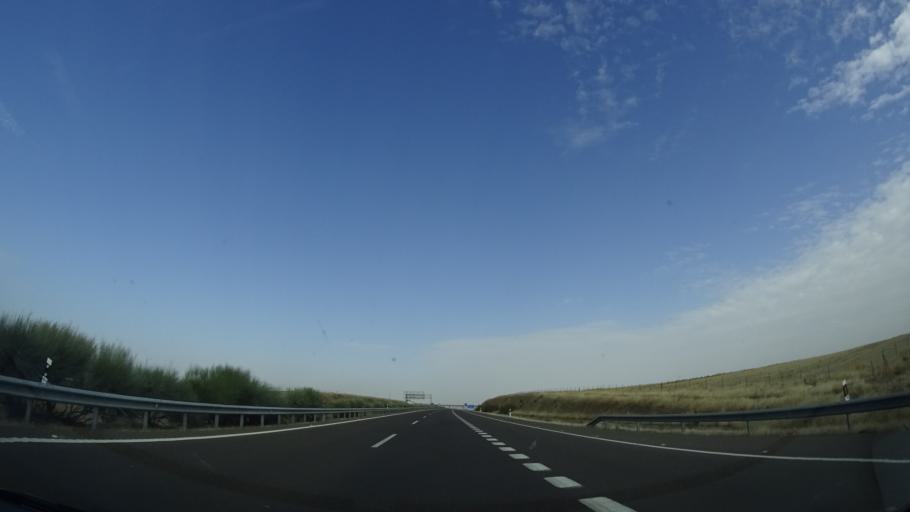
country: ES
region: Extremadura
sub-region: Provincia de Badajoz
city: Fuente de Cantos
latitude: 38.2664
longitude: -6.2977
